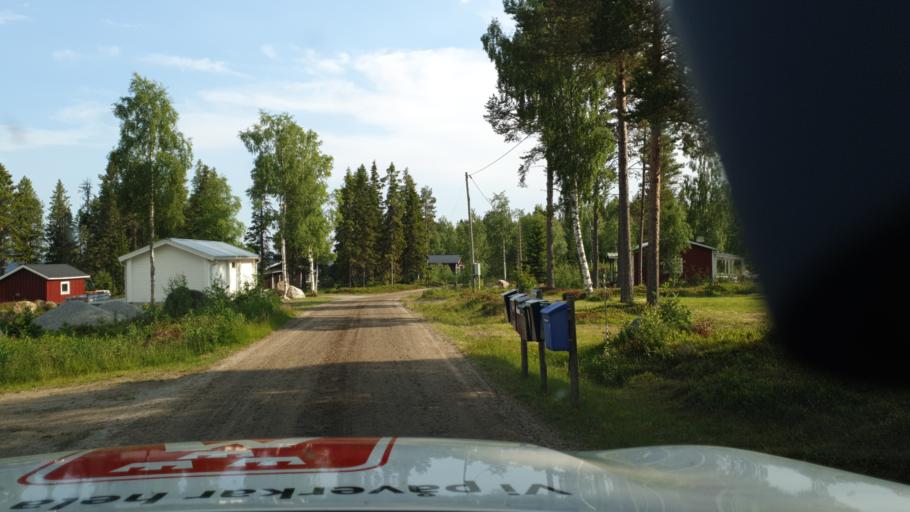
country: SE
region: Vaesterbotten
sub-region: Robertsfors Kommun
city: Robertsfors
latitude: 64.2111
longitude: 21.0779
